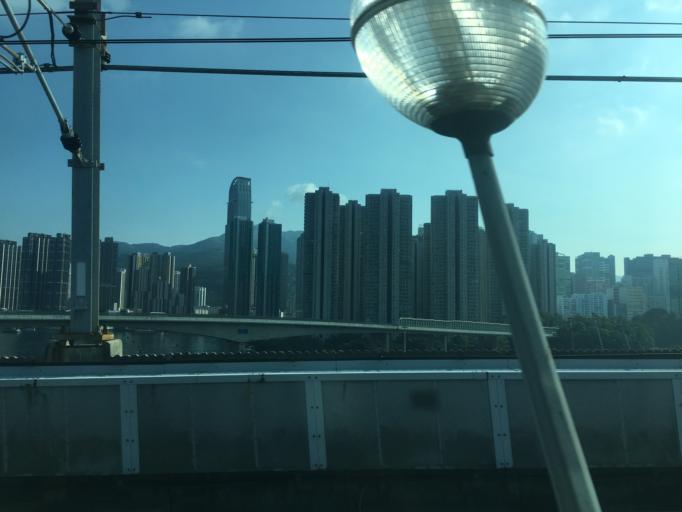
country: HK
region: Tsuen Wan
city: Tsuen Wan
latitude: 22.3575
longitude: 114.1106
